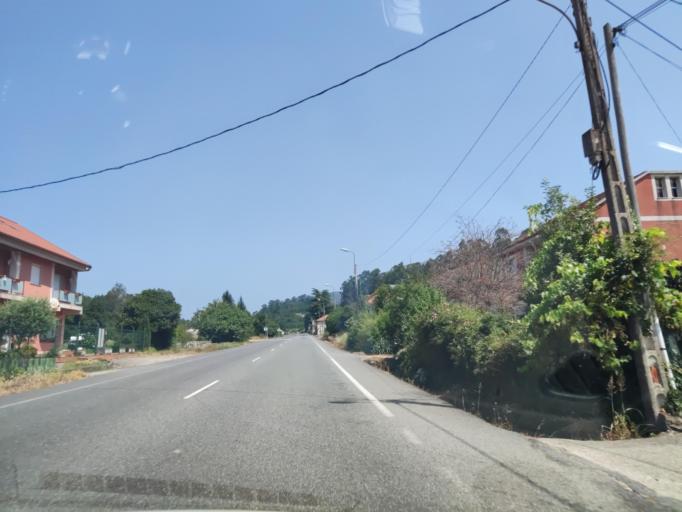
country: ES
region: Galicia
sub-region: Provincia de Pontevedra
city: Porrino
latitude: 42.2061
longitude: -8.6010
